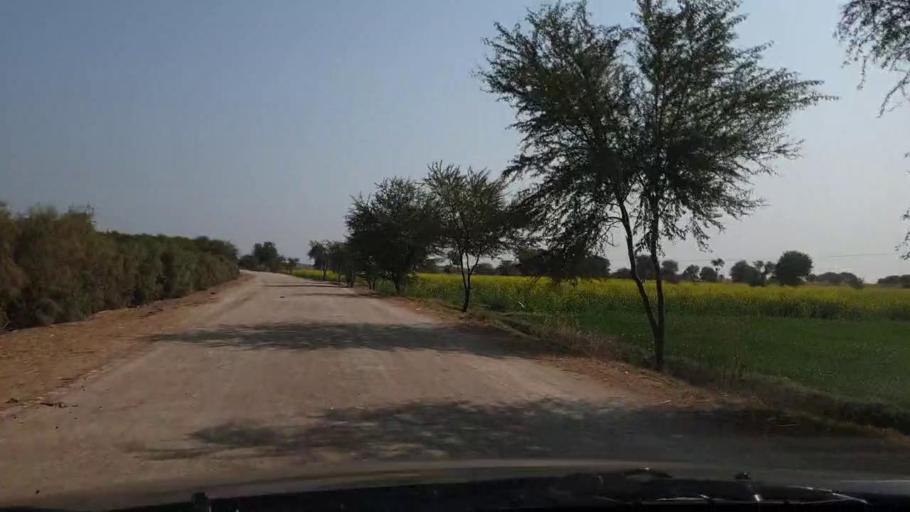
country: PK
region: Sindh
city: Jhol
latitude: 25.9979
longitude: 68.9143
